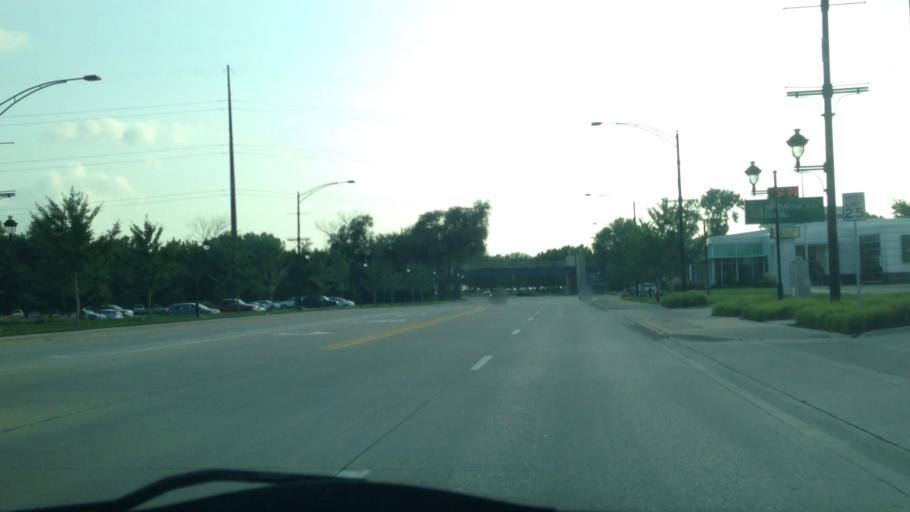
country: US
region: Iowa
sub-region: Johnson County
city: Coralville
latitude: 41.6686
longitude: -91.5665
